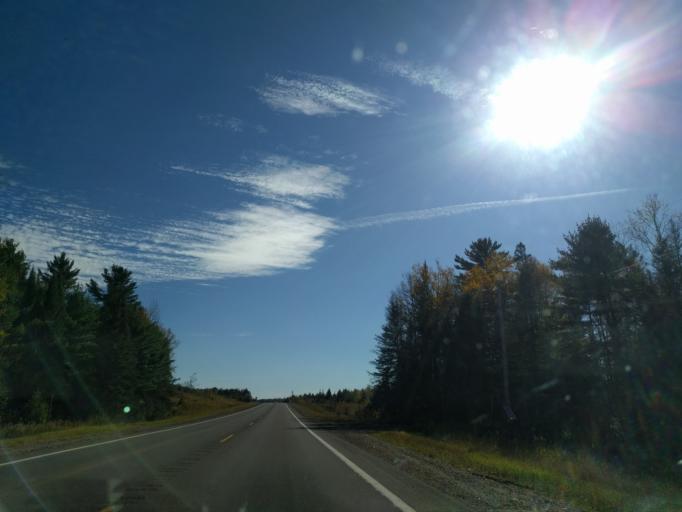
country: US
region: Michigan
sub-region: Marquette County
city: West Ishpeming
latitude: 46.3744
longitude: -87.9911
